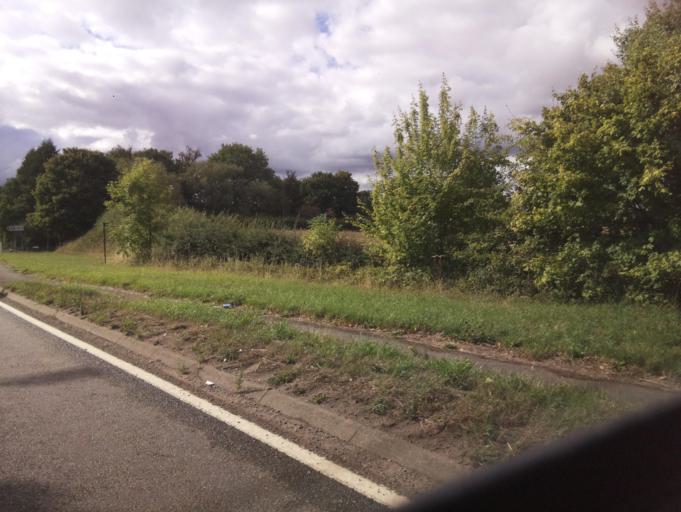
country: GB
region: England
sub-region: Leicestershire
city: Shepshed
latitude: 52.7605
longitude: -1.3152
